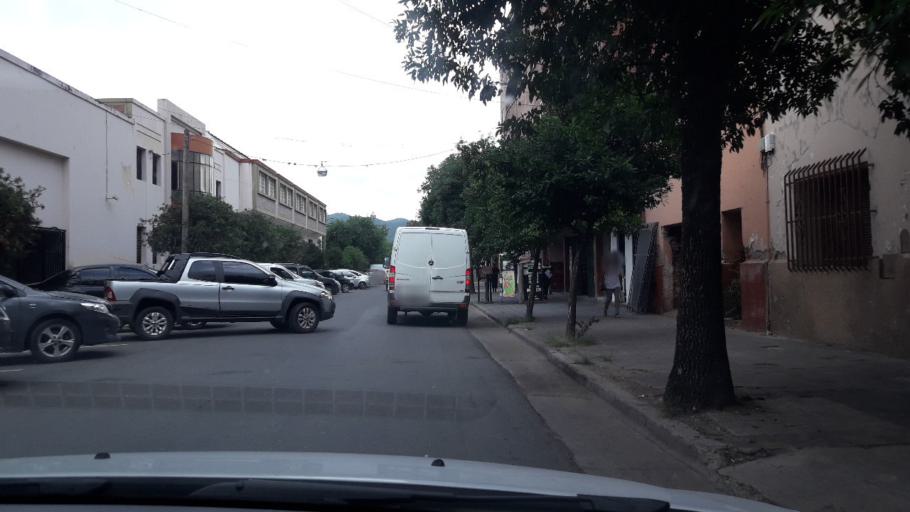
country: AR
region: Jujuy
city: San Salvador de Jujuy
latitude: -24.1815
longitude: -65.3129
